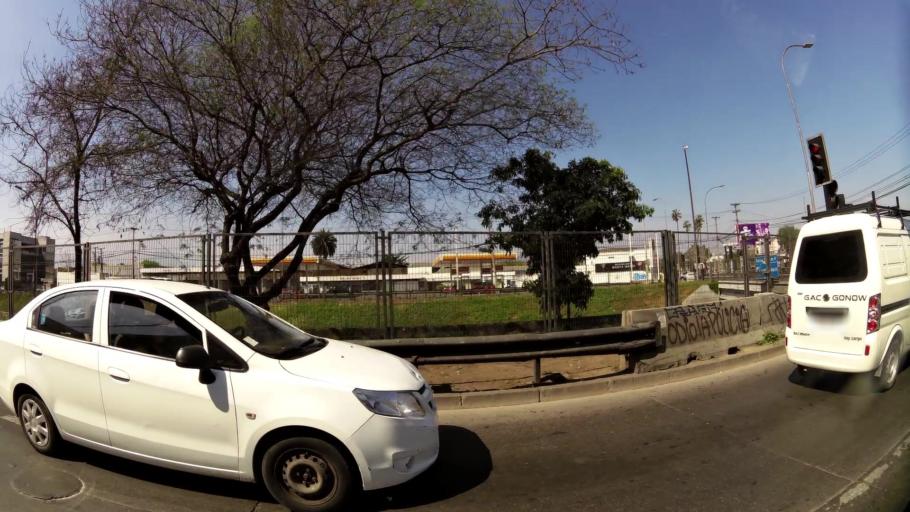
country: CL
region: Santiago Metropolitan
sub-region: Provincia de Santiago
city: Santiago
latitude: -33.4135
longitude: -70.6796
